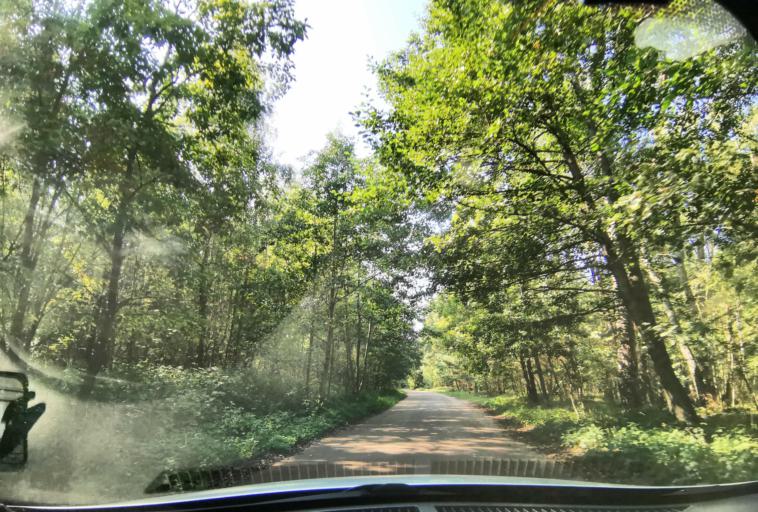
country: LT
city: Nida
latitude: 55.1618
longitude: 20.8270
